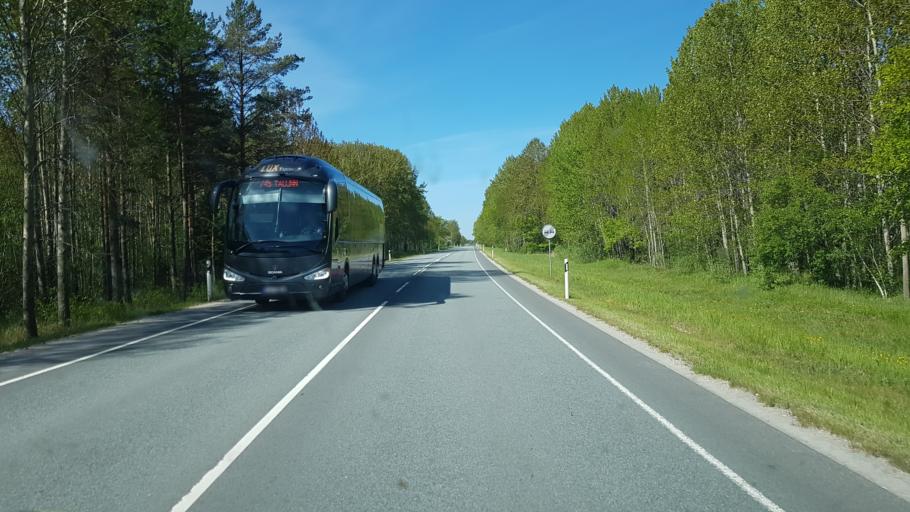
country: EE
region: Saare
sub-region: Kuressaare linn
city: Kuressaare
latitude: 58.3135
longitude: 22.6132
